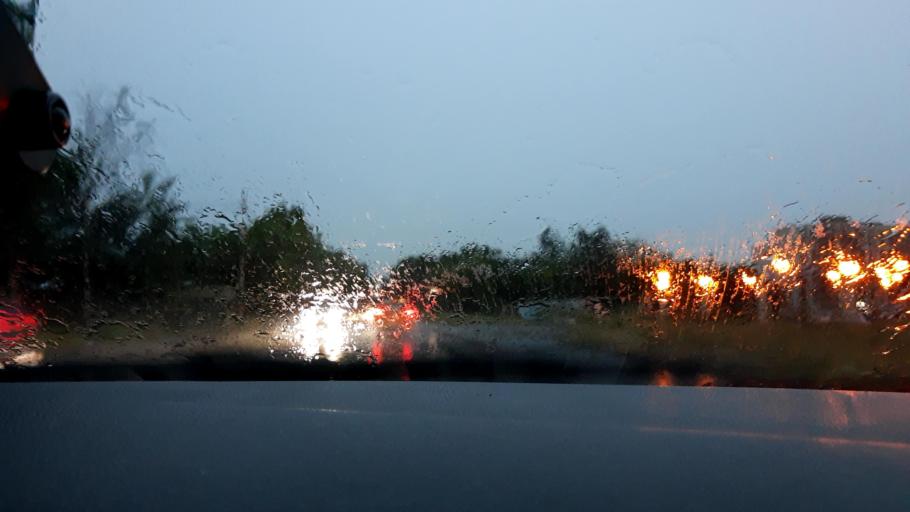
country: RU
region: Moskovskaya
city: Pirogovskiy
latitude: 55.9866
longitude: 37.7270
